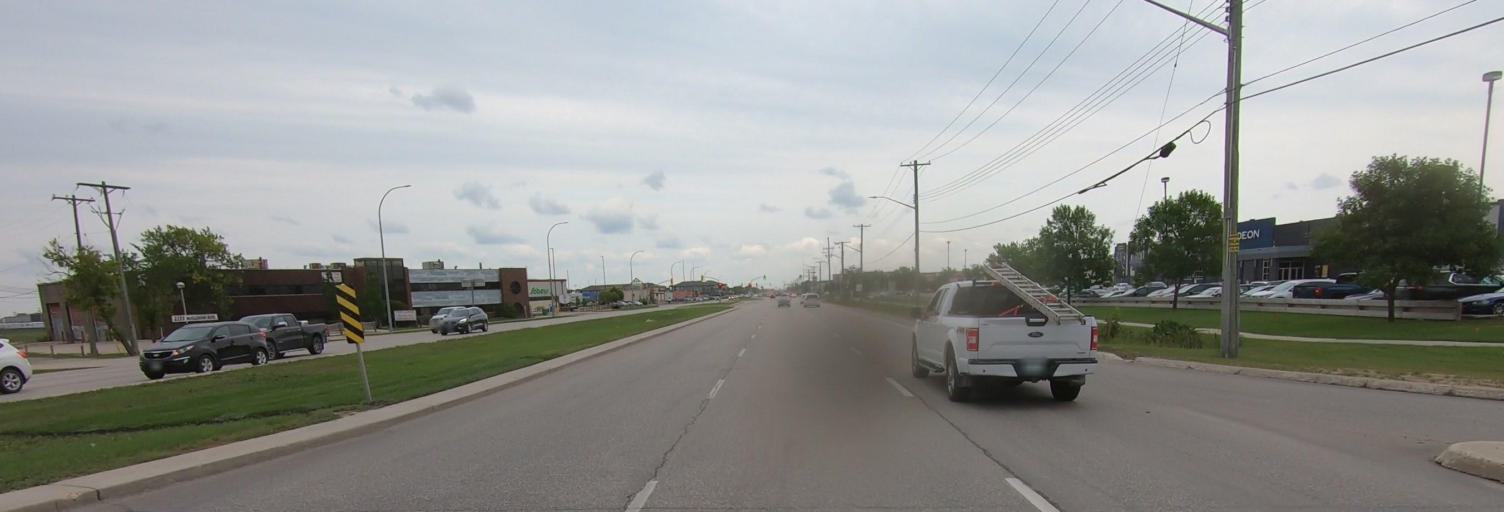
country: CA
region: Manitoba
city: Winnipeg
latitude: 49.8194
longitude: -97.2064
